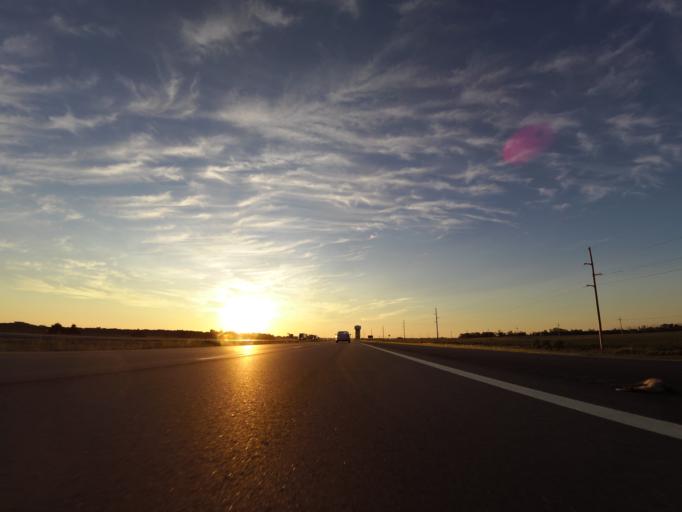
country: US
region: Kansas
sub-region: Reno County
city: South Hutchinson
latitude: 38.0132
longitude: -97.9563
